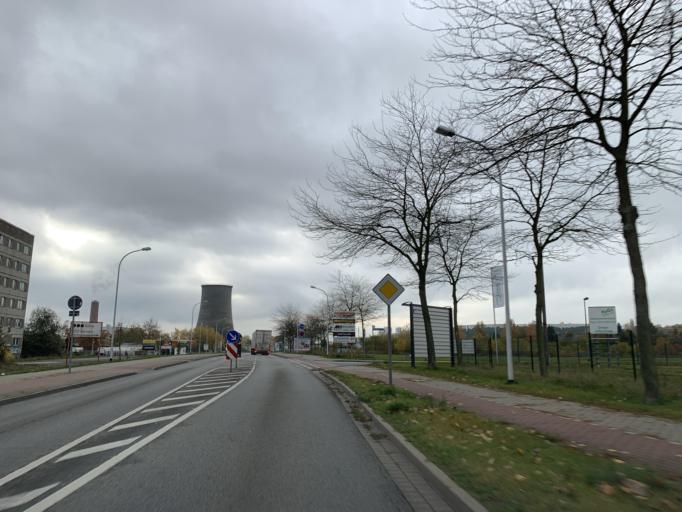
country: DE
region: Mecklenburg-Vorpommern
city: Neubrandenburg
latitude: 53.5775
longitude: 13.3015
